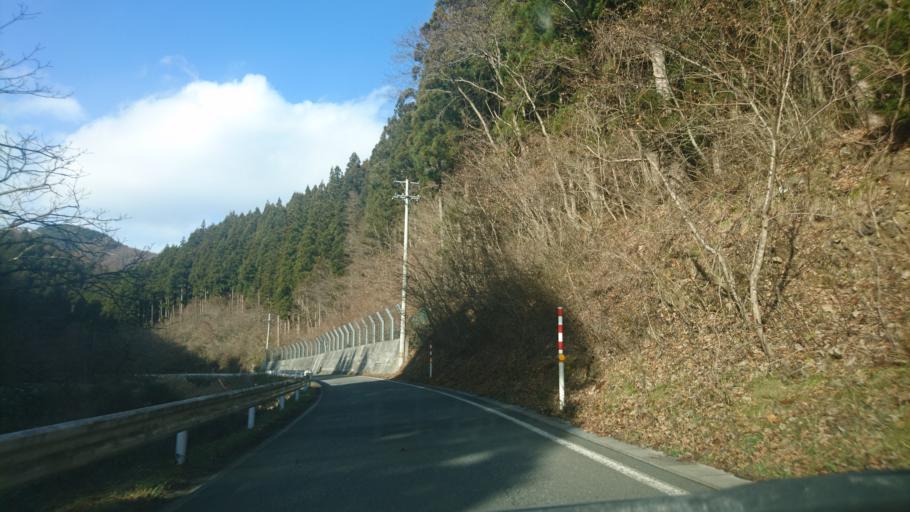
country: JP
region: Iwate
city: Mizusawa
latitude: 39.0958
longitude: 141.3860
